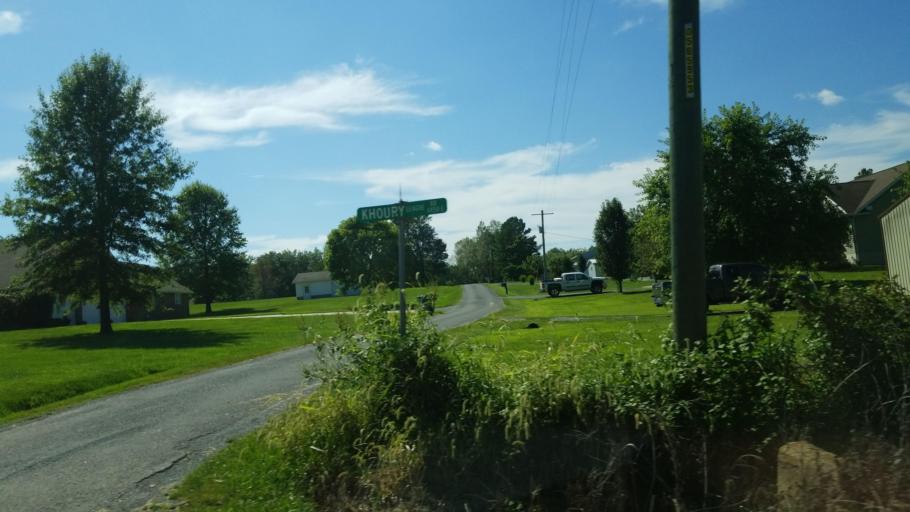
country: US
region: Illinois
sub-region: Williamson County
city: Marion
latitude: 37.7483
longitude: -88.8784
